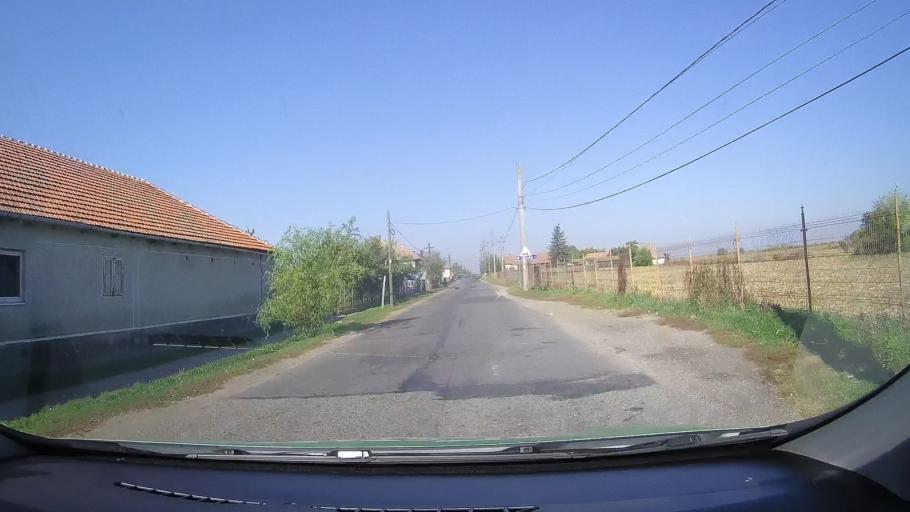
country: RO
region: Satu Mare
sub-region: Comuna Petresti
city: Petresti
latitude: 47.6052
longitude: 22.3627
